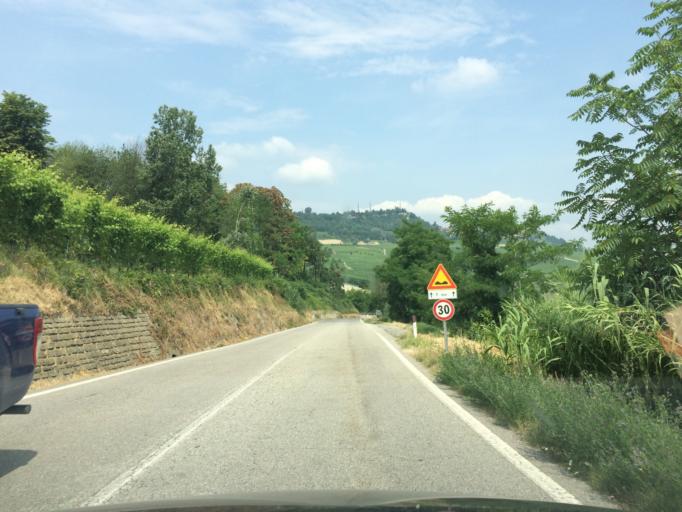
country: IT
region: Piedmont
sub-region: Provincia di Cuneo
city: Barolo
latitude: 44.6135
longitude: 7.9379
